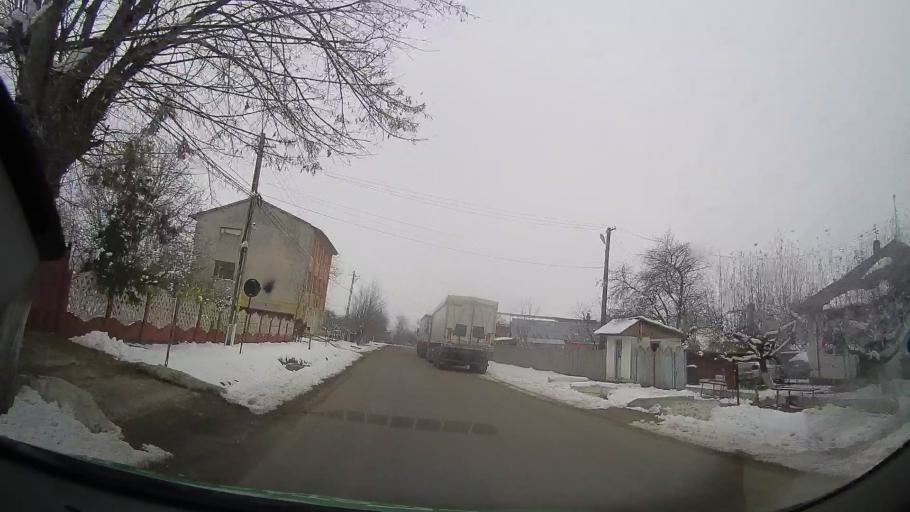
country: RO
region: Bacau
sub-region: Comuna Vultureni
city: Vultureni
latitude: 46.4037
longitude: 27.2730
